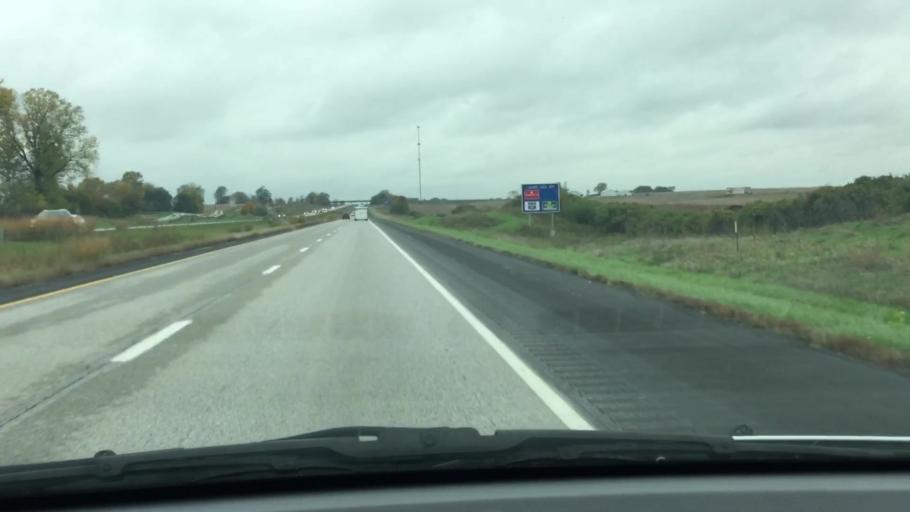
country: US
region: Iowa
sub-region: Iowa County
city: Williamsburg
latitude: 41.6874
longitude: -91.8389
